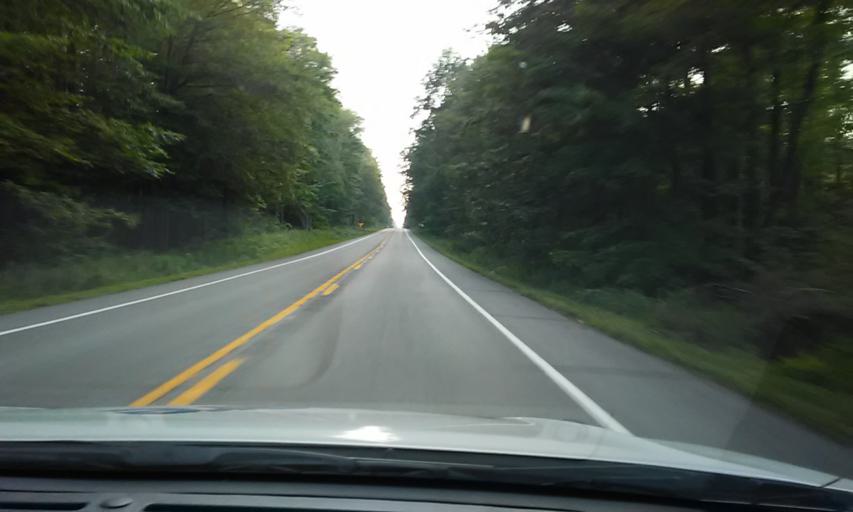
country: US
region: Pennsylvania
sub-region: Warren County
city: Sheffield
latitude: 41.5682
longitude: -78.9778
